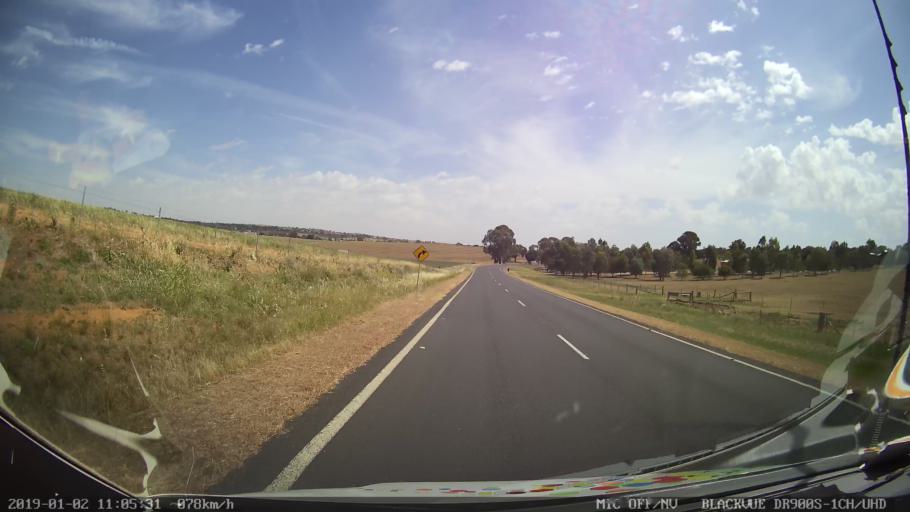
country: AU
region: New South Wales
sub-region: Young
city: Young
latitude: -34.5638
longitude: 148.3539
